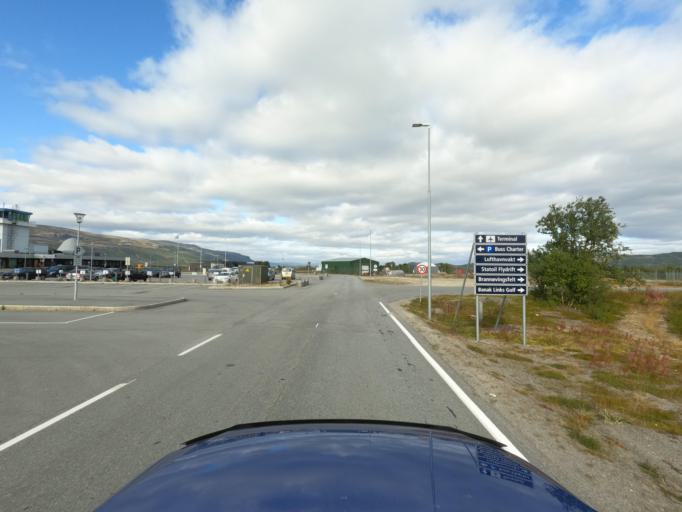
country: NO
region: Finnmark Fylke
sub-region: Porsanger
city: Lakselv
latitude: 70.0657
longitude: 24.9846
